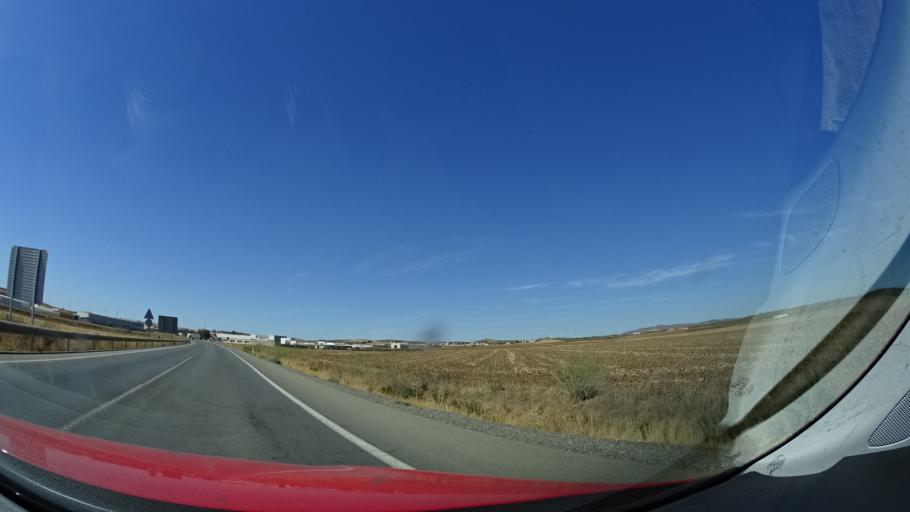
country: ES
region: Andalusia
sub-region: Provincia de Malaga
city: Campillos
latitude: 37.0495
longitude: -4.8465
